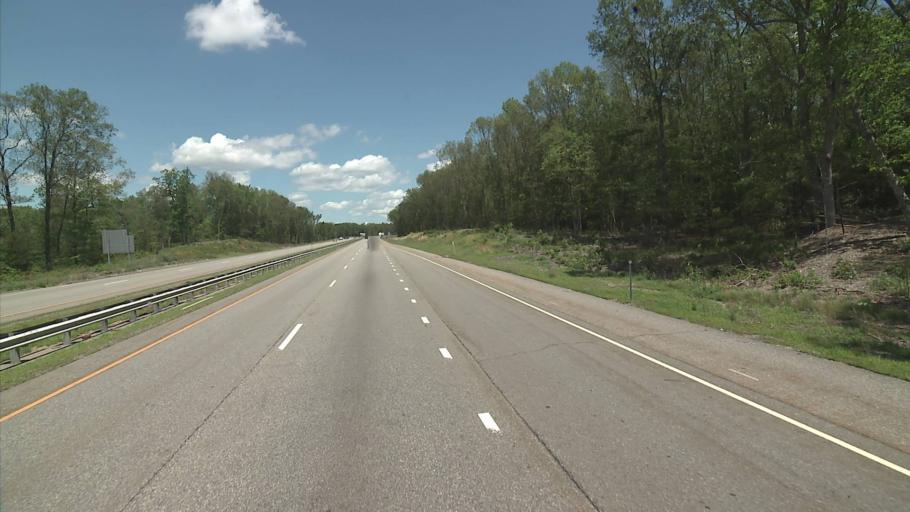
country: US
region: Connecticut
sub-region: New London County
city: Jewett City
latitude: 41.6176
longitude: -71.9450
